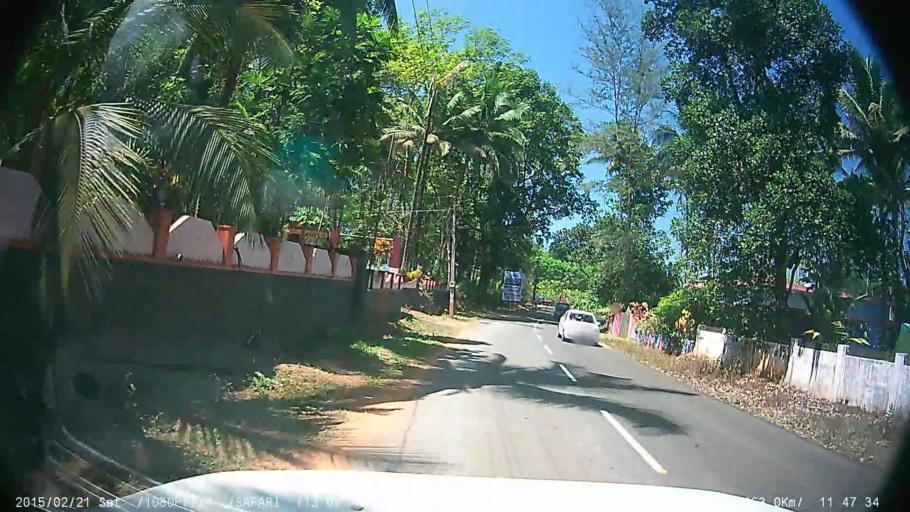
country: IN
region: Kerala
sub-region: Kottayam
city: Lalam
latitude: 9.7749
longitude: 76.7151
